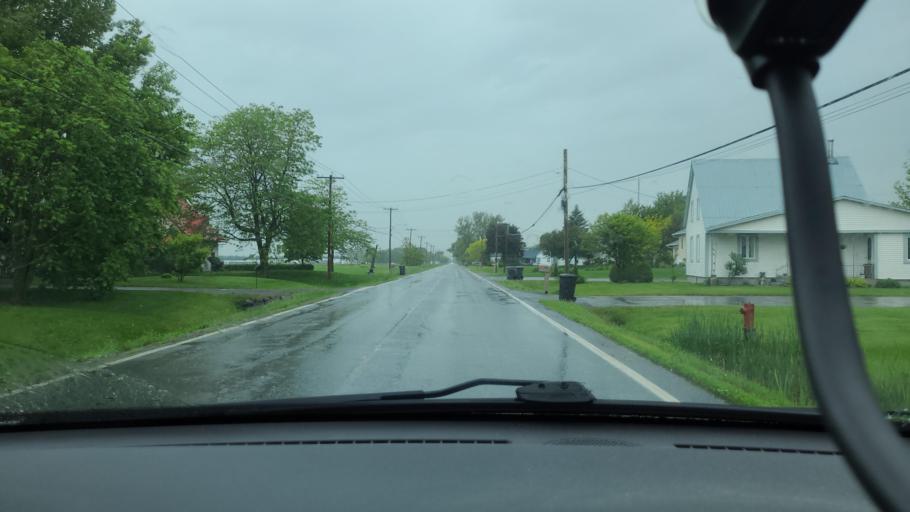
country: CA
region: Quebec
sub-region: Monteregie
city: Saint-Hyacinthe
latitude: 45.6169
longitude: -73.0147
